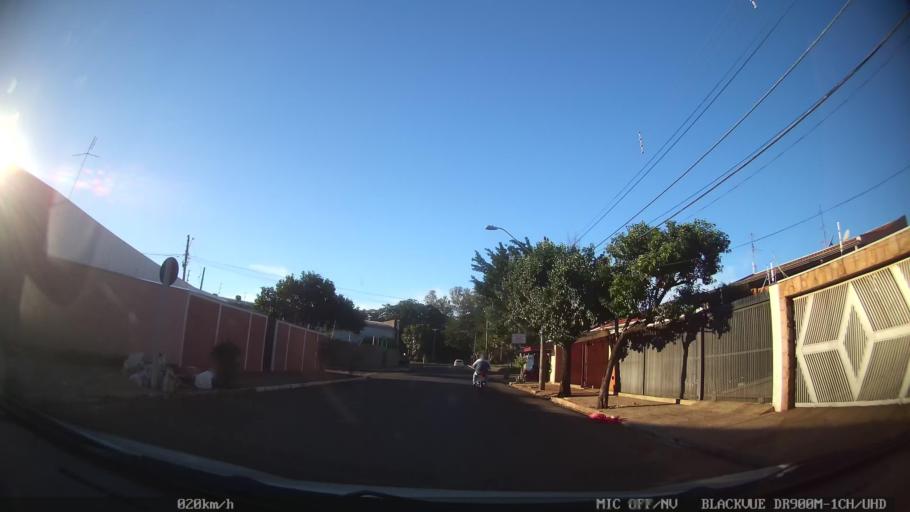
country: BR
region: Sao Paulo
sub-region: Araraquara
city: Araraquara
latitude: -21.8034
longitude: -48.1915
